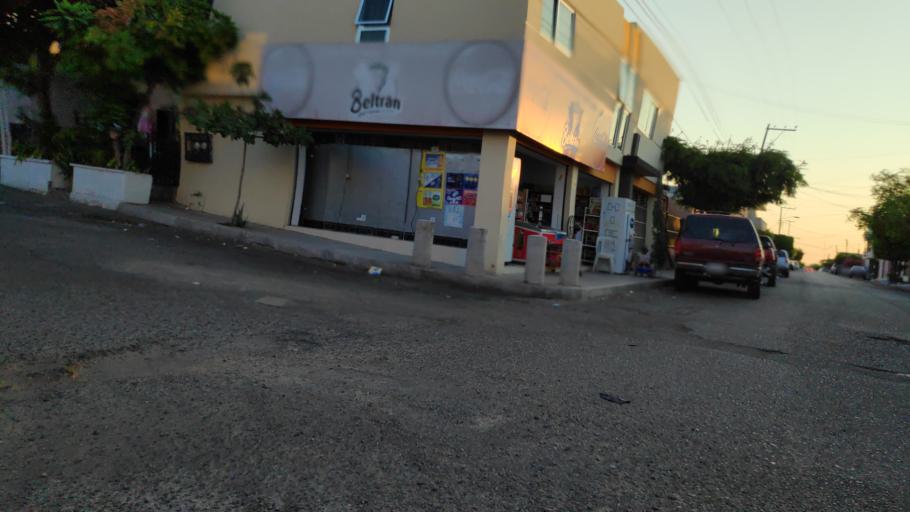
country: MX
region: Sinaloa
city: Culiacan
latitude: 24.7863
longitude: -107.4028
